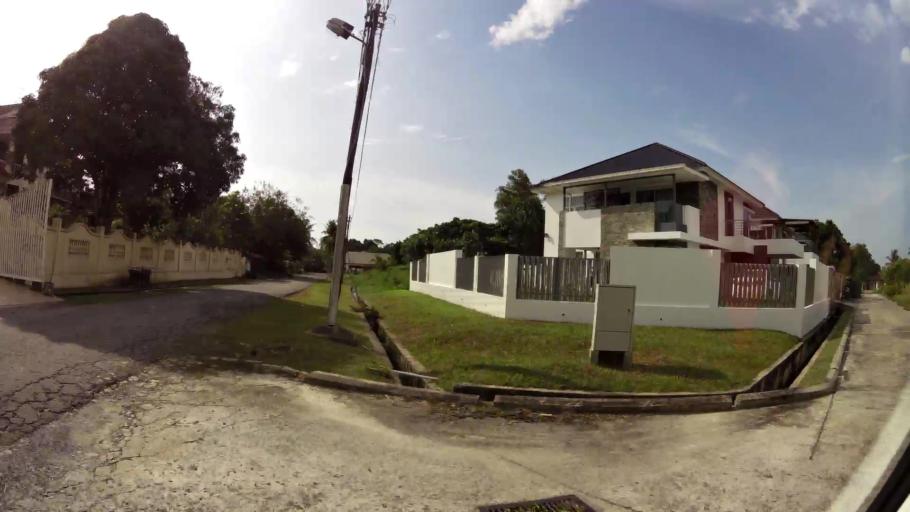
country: BN
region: Brunei and Muara
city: Bandar Seri Begawan
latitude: 4.9600
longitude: 114.9689
